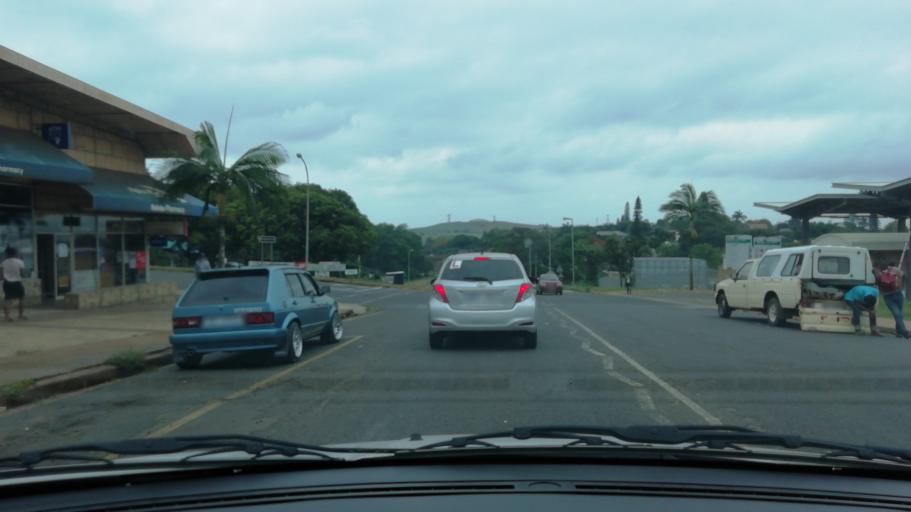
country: ZA
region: KwaZulu-Natal
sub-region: uThungulu District Municipality
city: Empangeni
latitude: -28.7395
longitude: 31.8955
